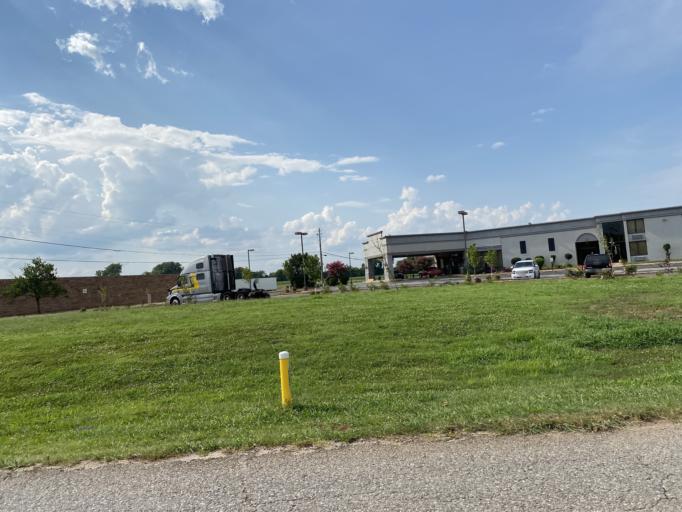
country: US
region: Alabama
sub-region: Madison County
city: Madison
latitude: 34.6798
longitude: -86.7442
